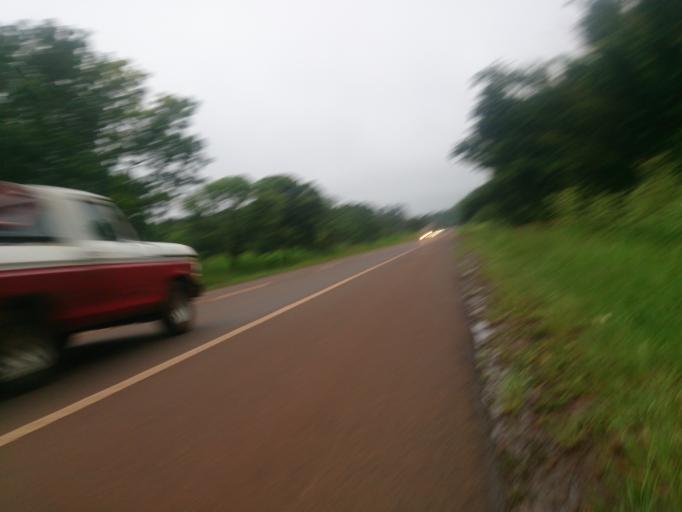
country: AR
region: Misiones
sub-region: Departamento de Obera
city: Obera
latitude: -27.4554
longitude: -55.0850
